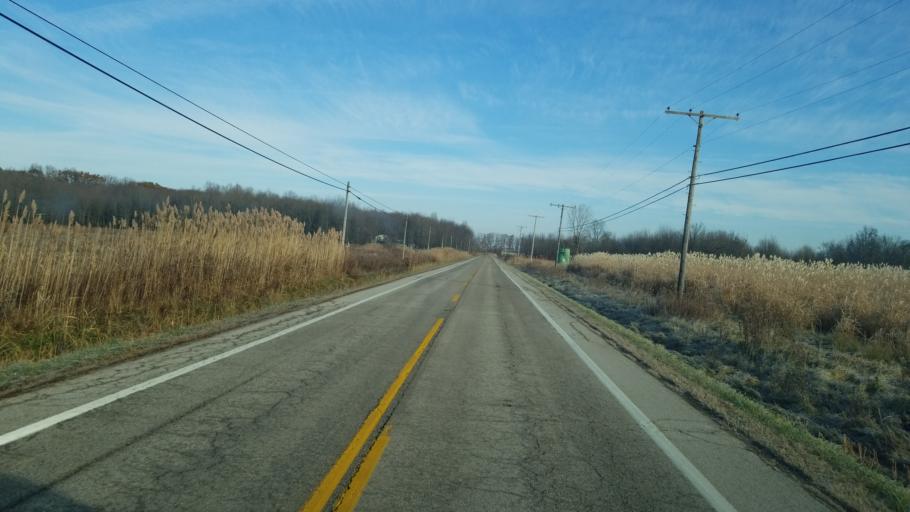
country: US
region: Ohio
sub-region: Ashtabula County
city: Jefferson
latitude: 41.7232
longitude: -80.6690
